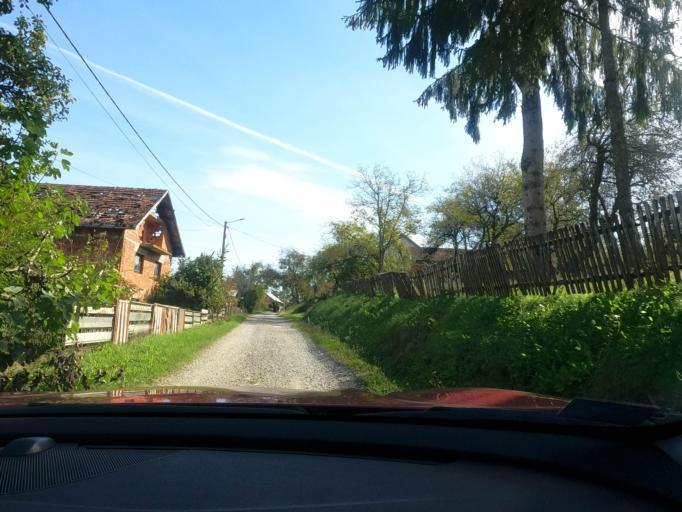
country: HR
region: Sisacko-Moslavacka
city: Petrinja
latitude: 45.3411
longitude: 16.2399
